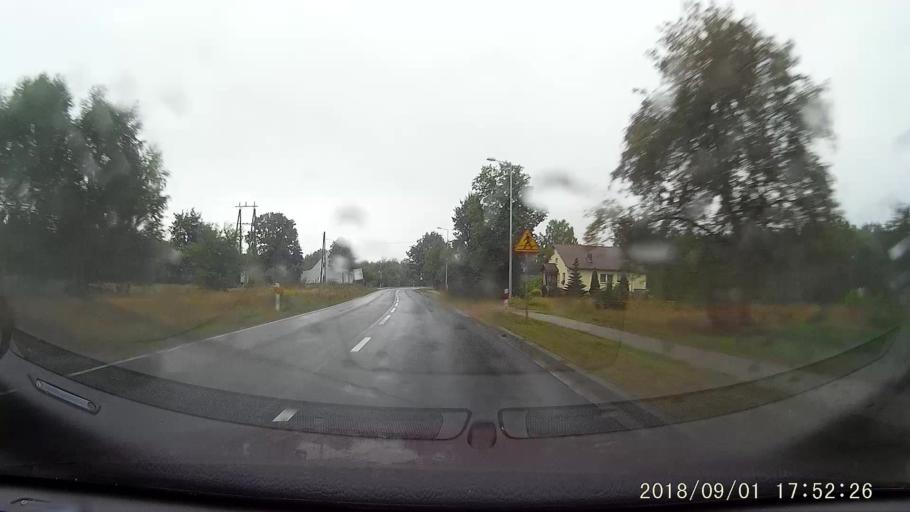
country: PL
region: Lubusz
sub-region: Powiat zaganski
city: Ilowa
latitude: 51.4894
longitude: 15.1940
